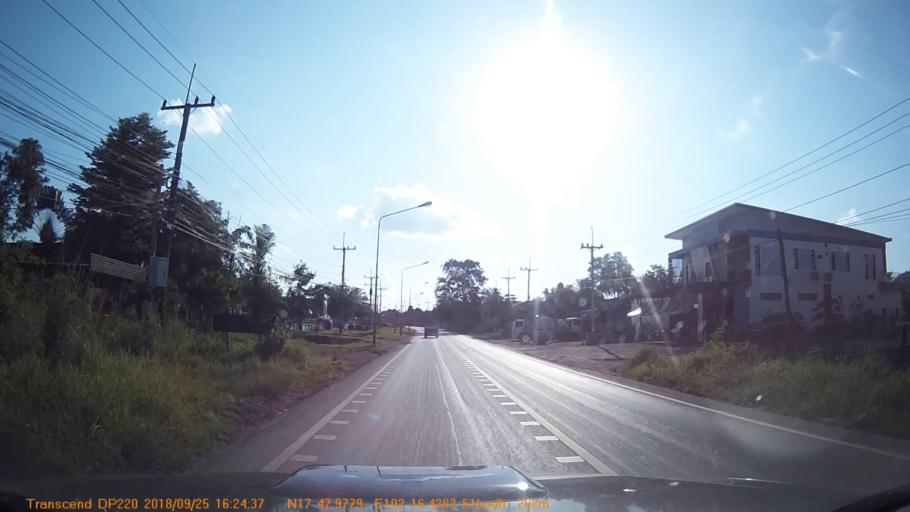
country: TH
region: Changwat Udon Thani
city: Nam Som
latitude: 17.7996
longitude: 102.2737
